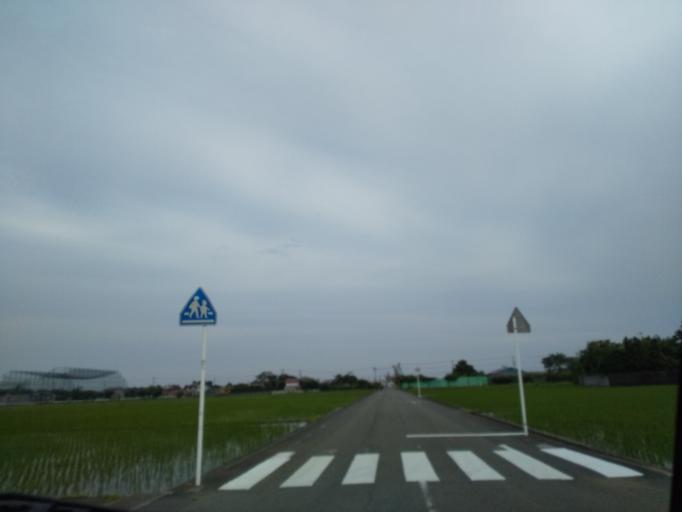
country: JP
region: Kanagawa
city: Zama
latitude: 35.4787
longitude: 139.3551
